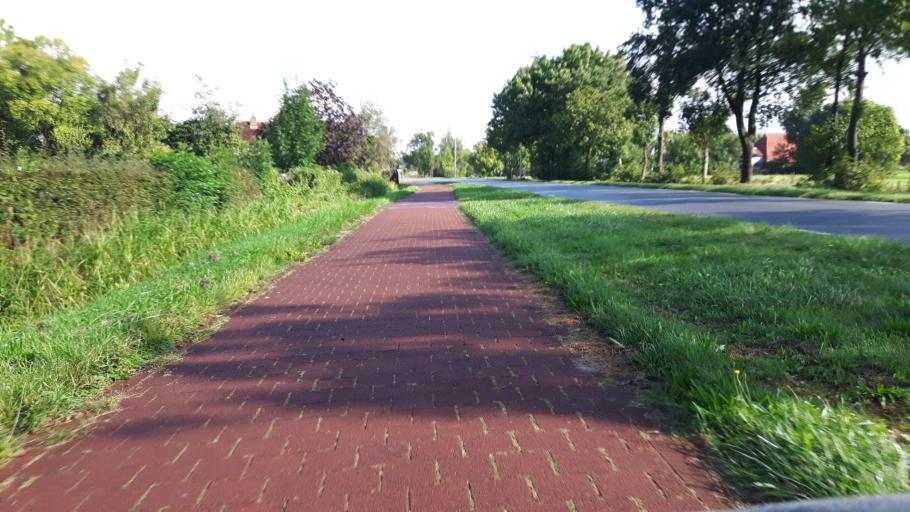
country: NL
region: Friesland
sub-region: Gemeente Smallingerland
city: Drachten
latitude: 53.0798
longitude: 6.0993
